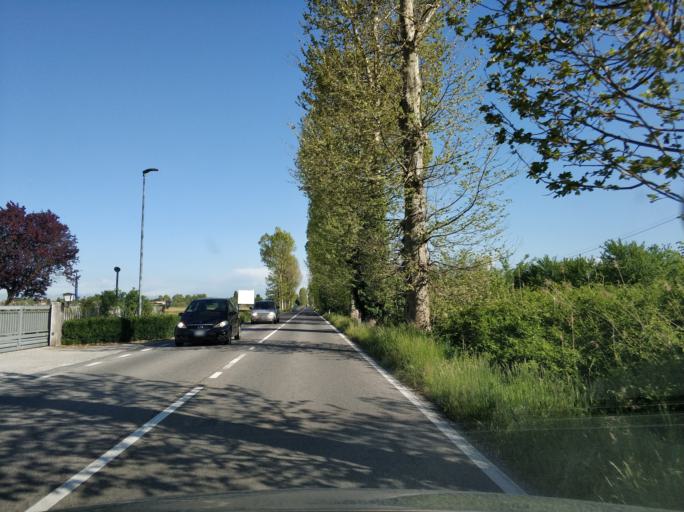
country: IT
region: Friuli Venezia Giulia
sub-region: Provincia di Udine
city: Terzo d'Aquileia
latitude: 45.7897
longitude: 13.3568
